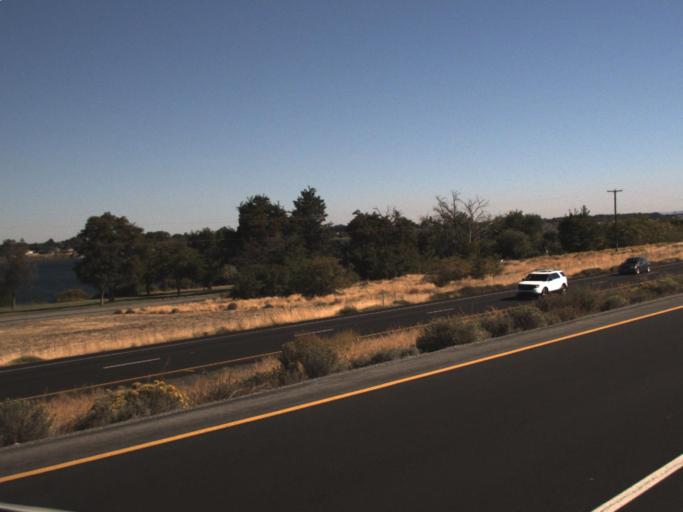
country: US
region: Washington
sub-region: Franklin County
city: West Pasco
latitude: 46.2258
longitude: -119.1772
